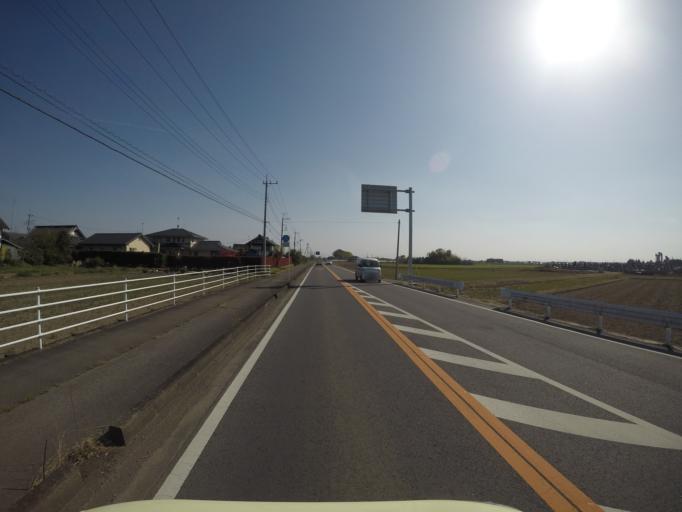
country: JP
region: Tochigi
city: Kaminokawa
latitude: 36.3695
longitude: 139.9081
